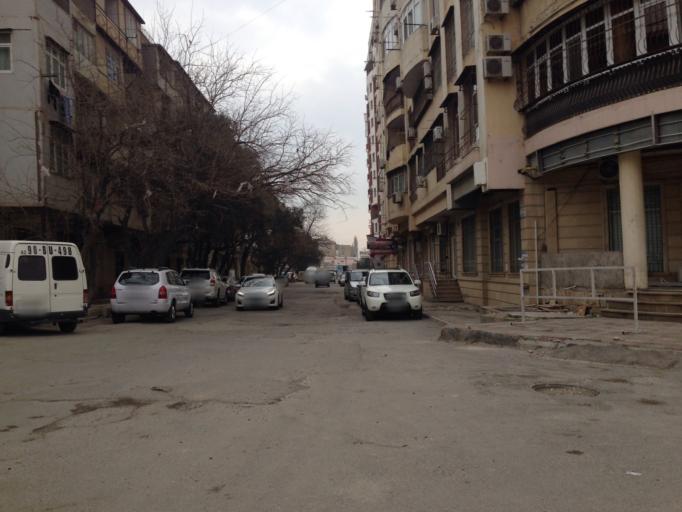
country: AZ
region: Baki
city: Baku
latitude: 40.3969
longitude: 49.8749
